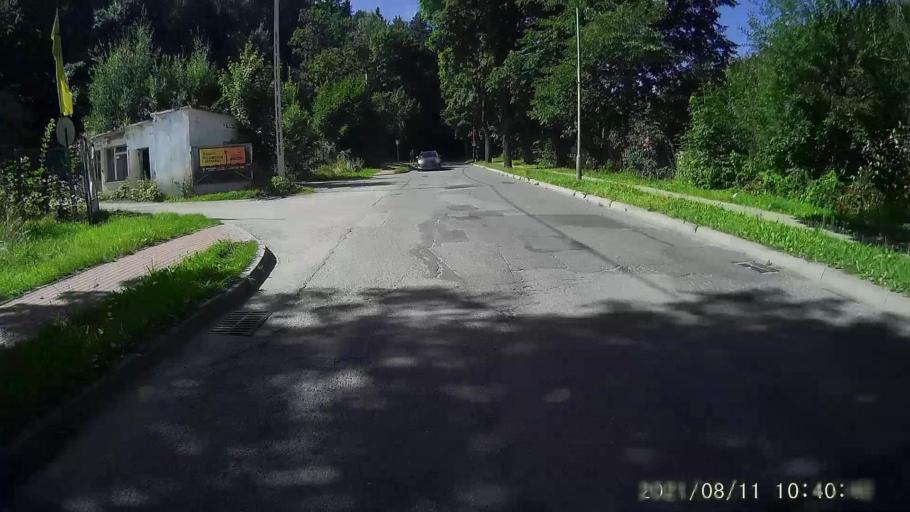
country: PL
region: Lower Silesian Voivodeship
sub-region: Powiat klodzki
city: Polanica-Zdroj
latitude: 50.3982
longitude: 16.5042
